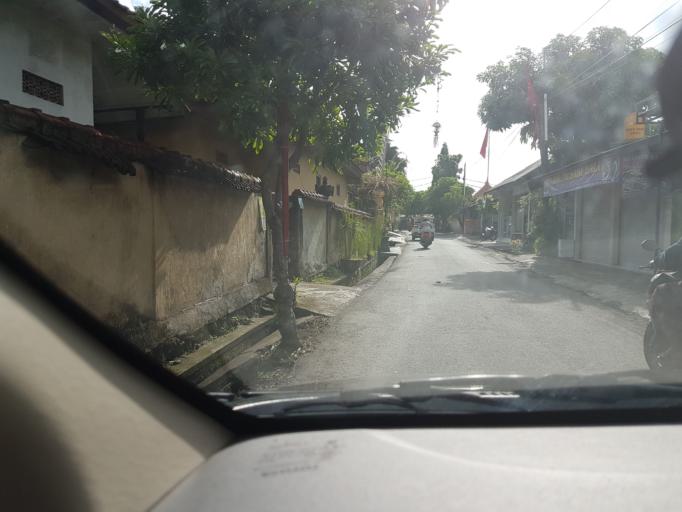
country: ID
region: Bali
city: Kuta
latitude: -8.6833
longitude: 115.1767
